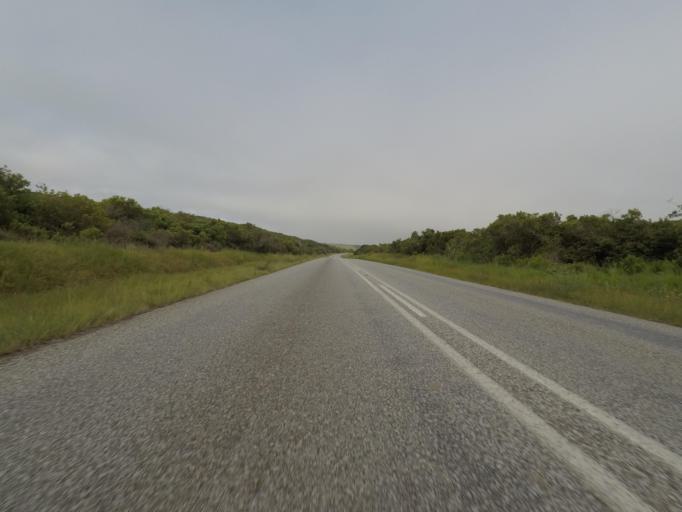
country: ZA
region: Eastern Cape
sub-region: Cacadu District Municipality
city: Port Alfred
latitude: -33.6071
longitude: 26.8221
